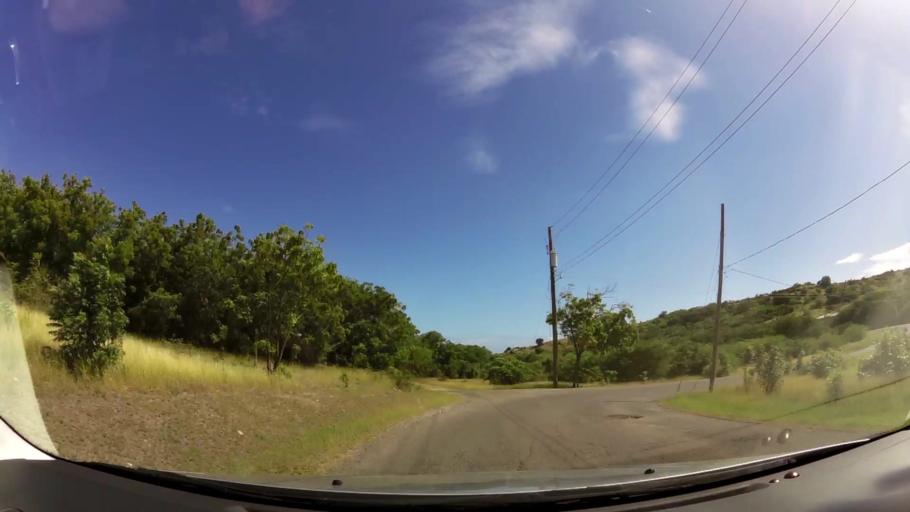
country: AG
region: Saint Paul
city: Falmouth
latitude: 17.0343
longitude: -61.7471
